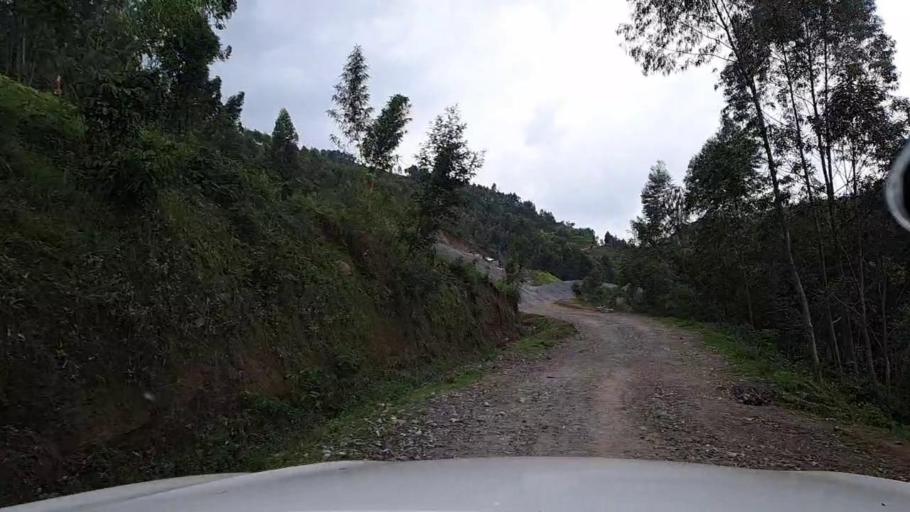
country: RW
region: Northern Province
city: Byumba
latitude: -1.6265
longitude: 29.9240
